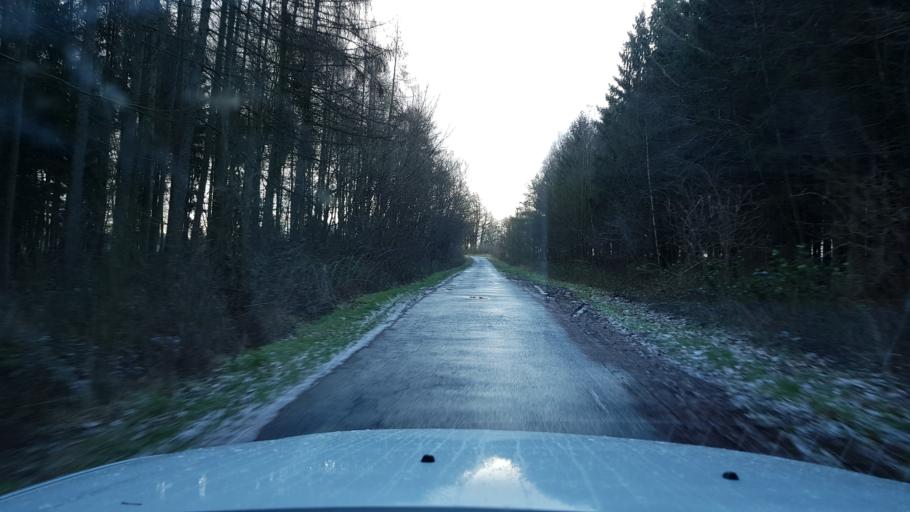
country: PL
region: West Pomeranian Voivodeship
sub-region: Powiat gryficki
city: Trzebiatow
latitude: 54.0413
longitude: 15.3407
